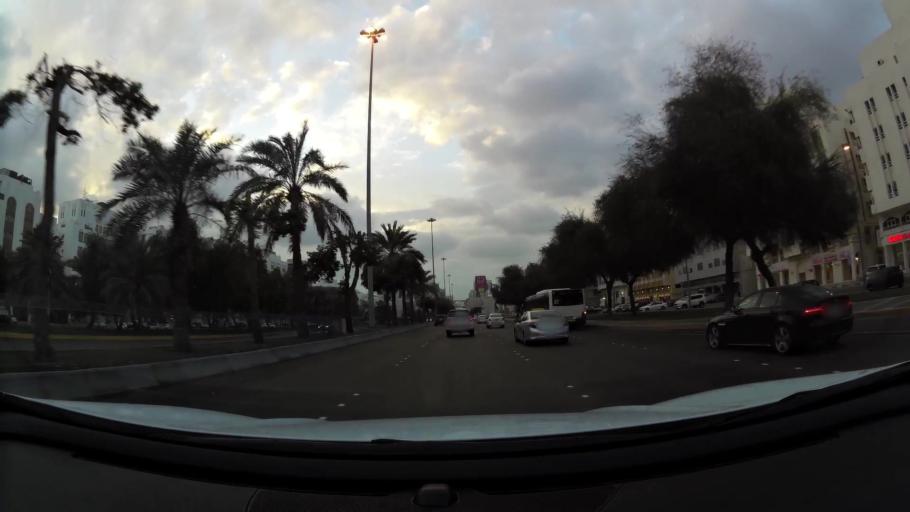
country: AE
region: Abu Dhabi
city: Abu Dhabi
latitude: 24.4536
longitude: 54.3866
